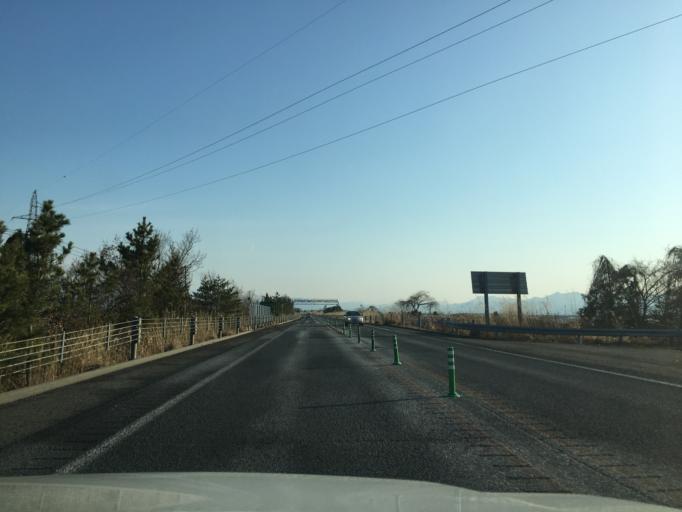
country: JP
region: Yamagata
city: Sagae
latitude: 38.3326
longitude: 140.2974
